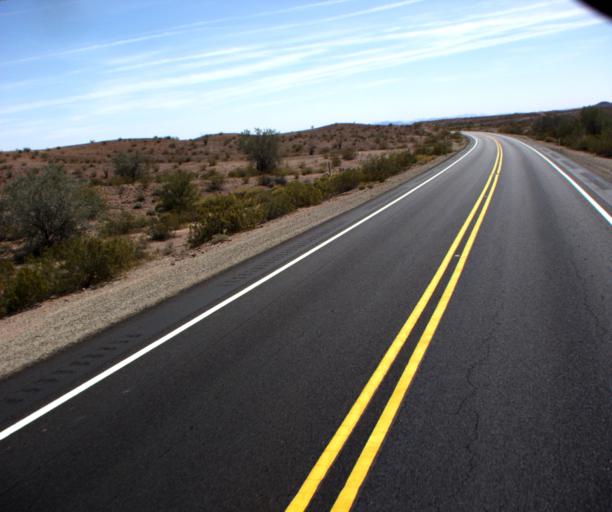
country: US
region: Arizona
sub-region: Yuma County
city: Wellton
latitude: 33.1010
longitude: -114.2981
